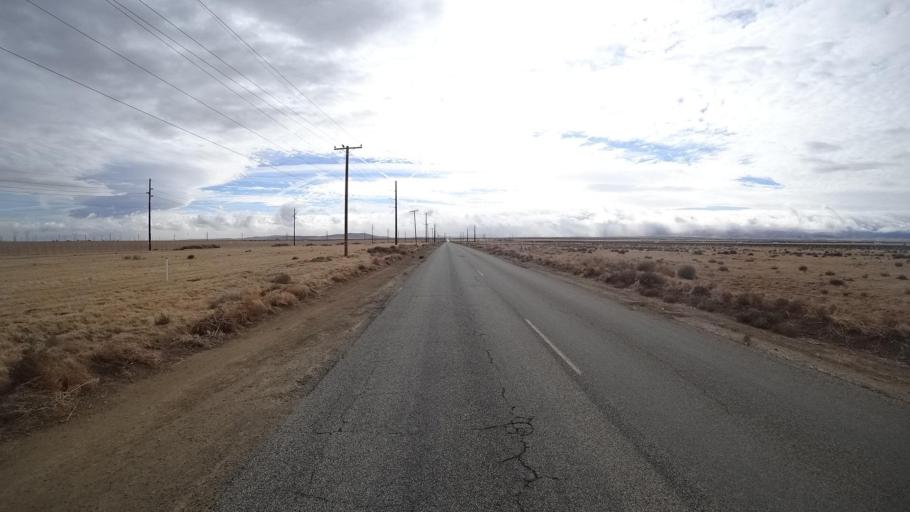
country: US
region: California
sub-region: Los Angeles County
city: Green Valley
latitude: 34.8310
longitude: -118.4317
